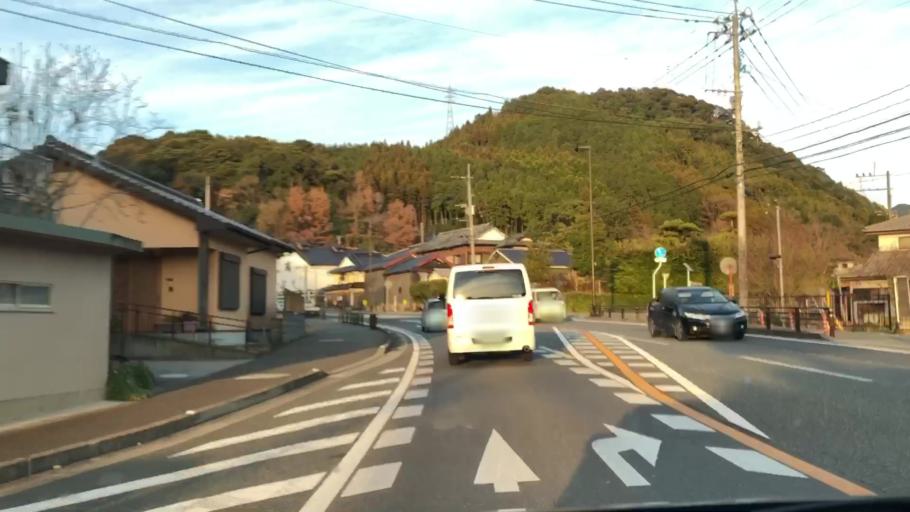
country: JP
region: Kumamoto
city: Minamata
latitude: 32.2343
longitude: 130.4649
